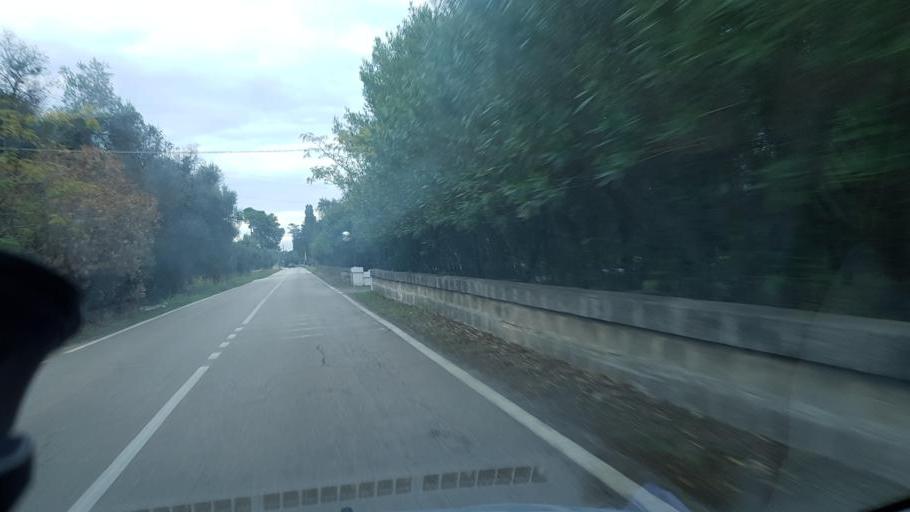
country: IT
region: Apulia
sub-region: Provincia di Brindisi
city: Oria
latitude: 40.5172
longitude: 17.6752
